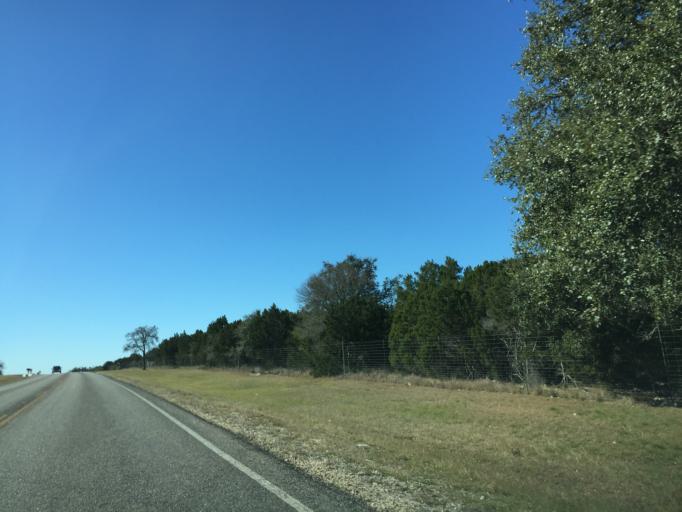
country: US
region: Texas
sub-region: Comal County
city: Garden Ridge
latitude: 29.7372
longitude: -98.3054
